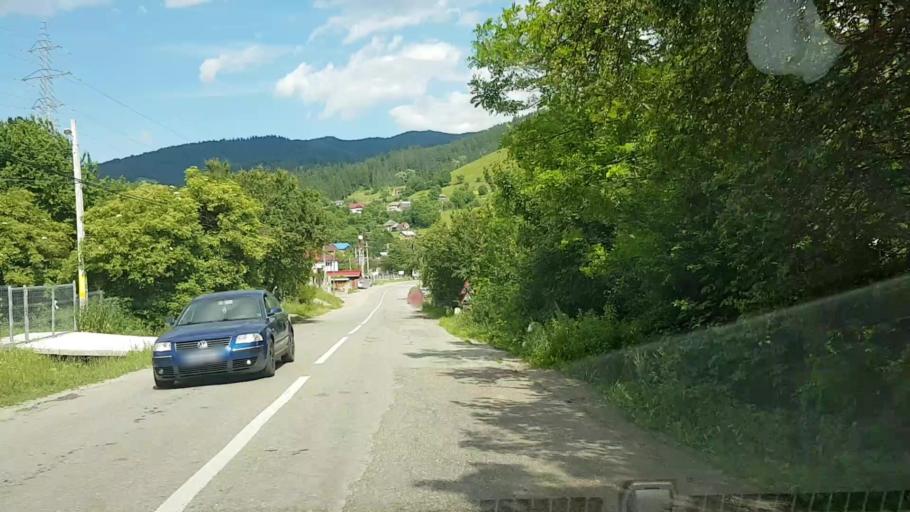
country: RO
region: Neamt
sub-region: Comuna Hangu
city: Hangu
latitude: 47.0184
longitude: 26.0837
